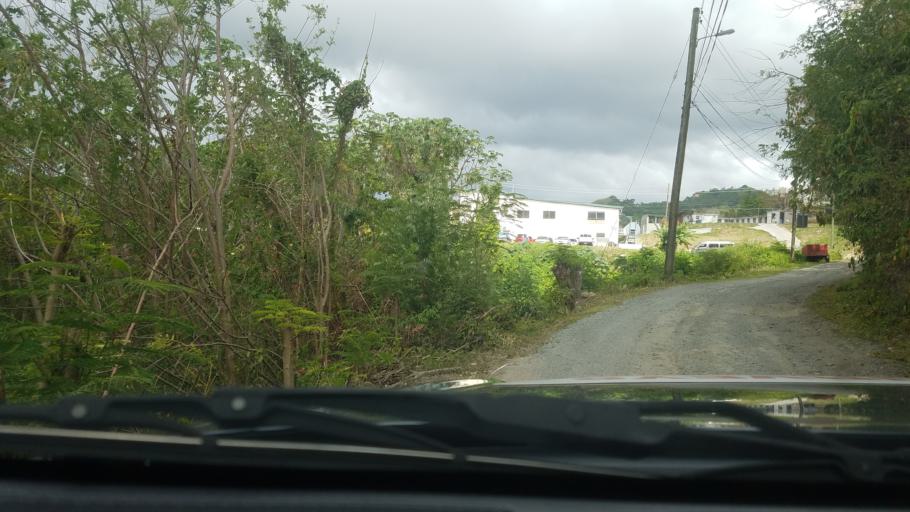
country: LC
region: Castries Quarter
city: Bisee
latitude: 14.0194
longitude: -60.9877
